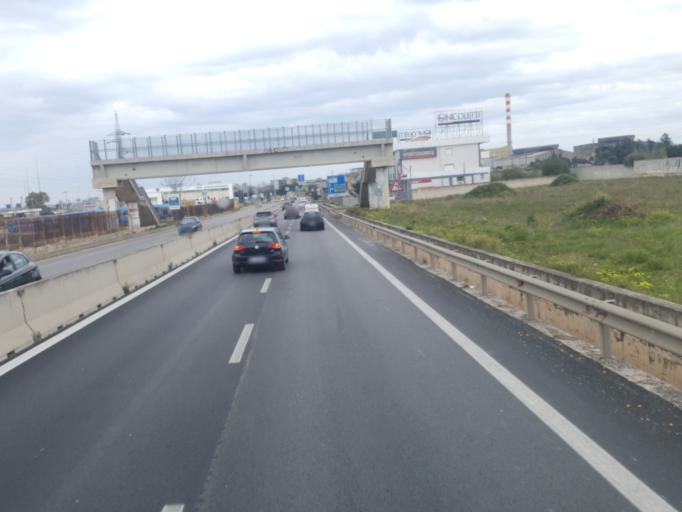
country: IT
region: Apulia
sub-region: Provincia di Bari
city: Modugno
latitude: 41.1033
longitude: 16.8111
